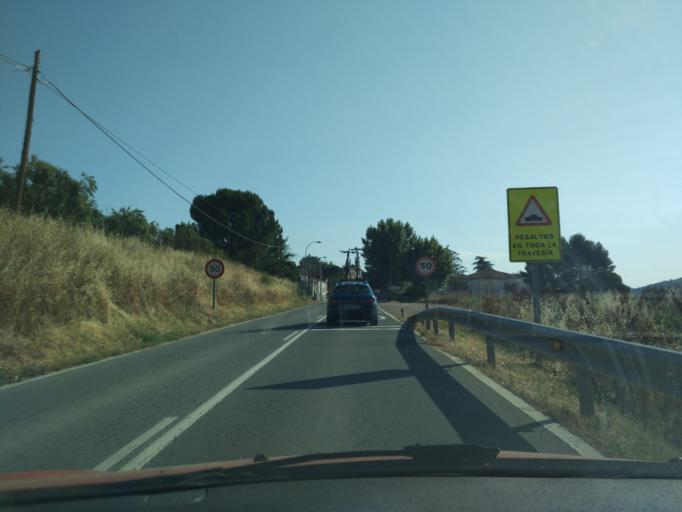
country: ES
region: Madrid
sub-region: Provincia de Madrid
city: Ambite
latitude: 40.3252
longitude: -3.1849
